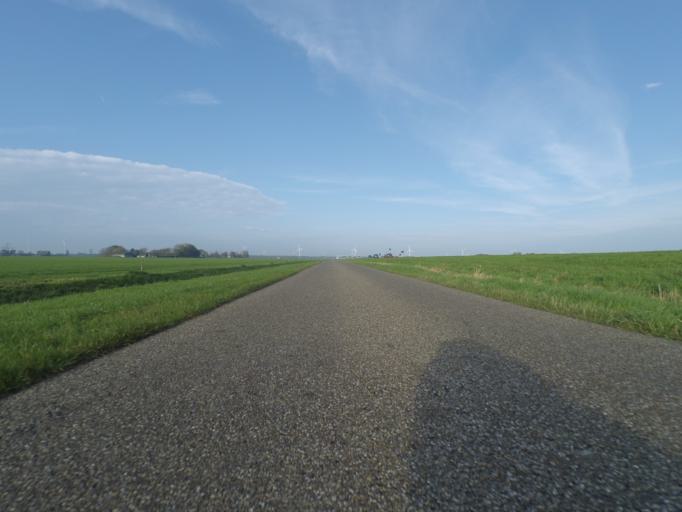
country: NL
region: Gelderland
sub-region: Gemeente Harderwijk
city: Harderwijk
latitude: 52.3826
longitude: 5.5862
